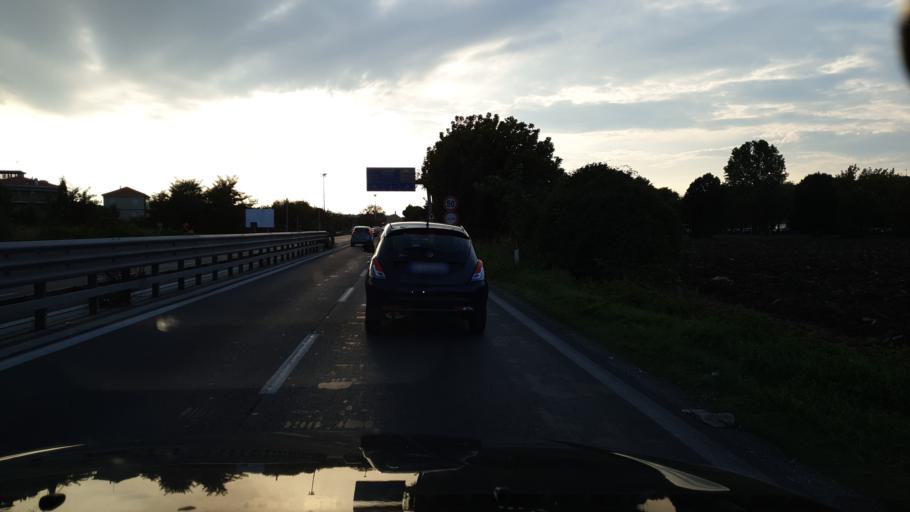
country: IT
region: Emilia-Romagna
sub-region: Provincia di Rimini
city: Rimini
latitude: 44.0418
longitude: 12.5786
